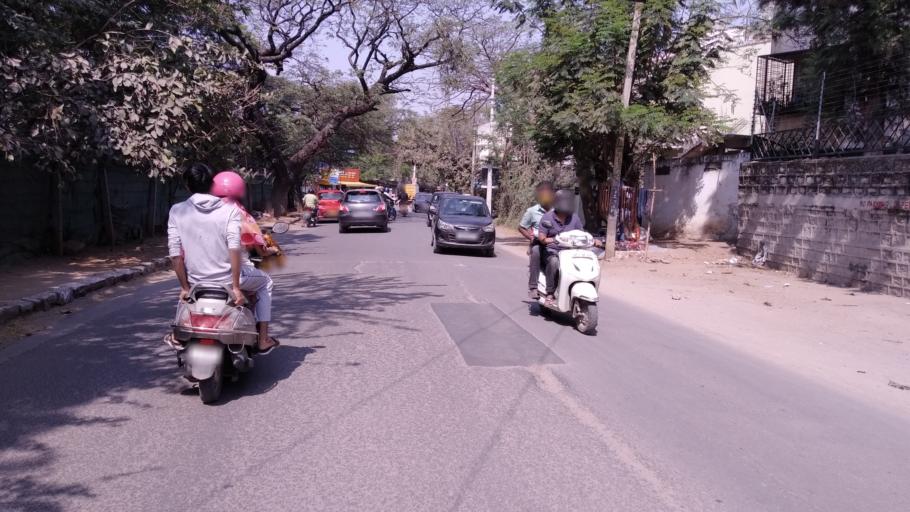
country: IN
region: Telangana
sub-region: Hyderabad
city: Malkajgiri
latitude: 17.4628
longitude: 78.4844
